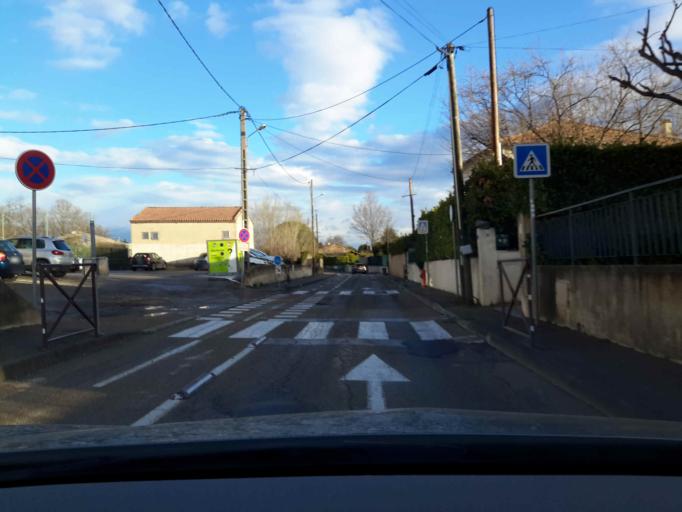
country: FR
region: Languedoc-Roussillon
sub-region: Departement du Gard
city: Generac
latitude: 43.7309
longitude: 4.3455
